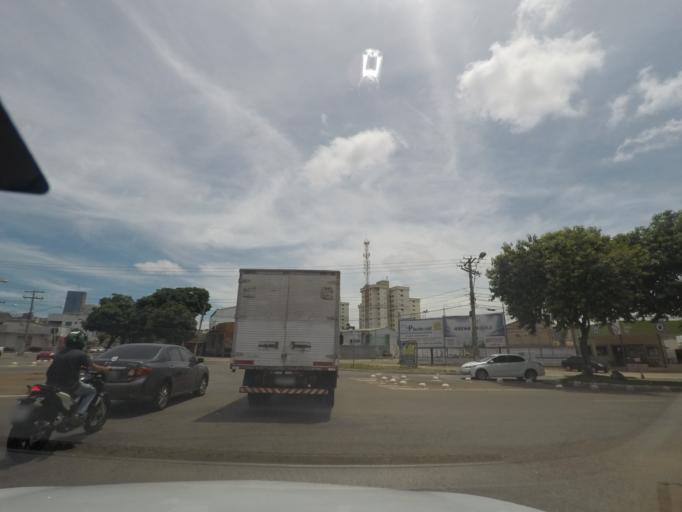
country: BR
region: Goias
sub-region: Goiania
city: Goiania
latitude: -16.6889
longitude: -49.2990
